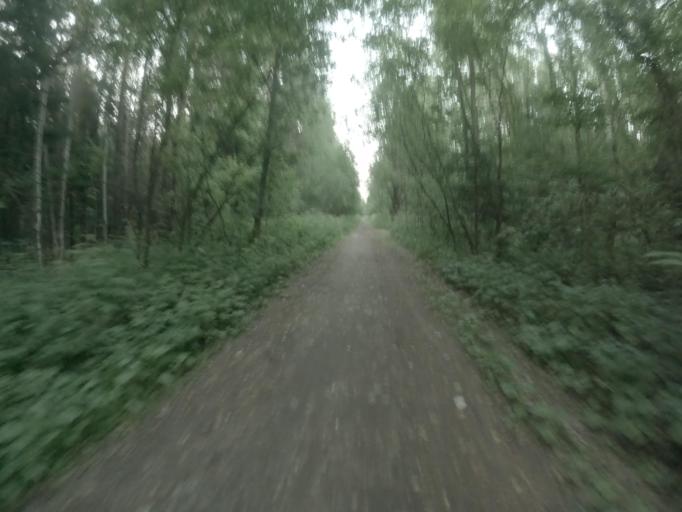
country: RU
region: St.-Petersburg
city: Krasnogvargeisky
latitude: 59.9600
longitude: 30.5362
